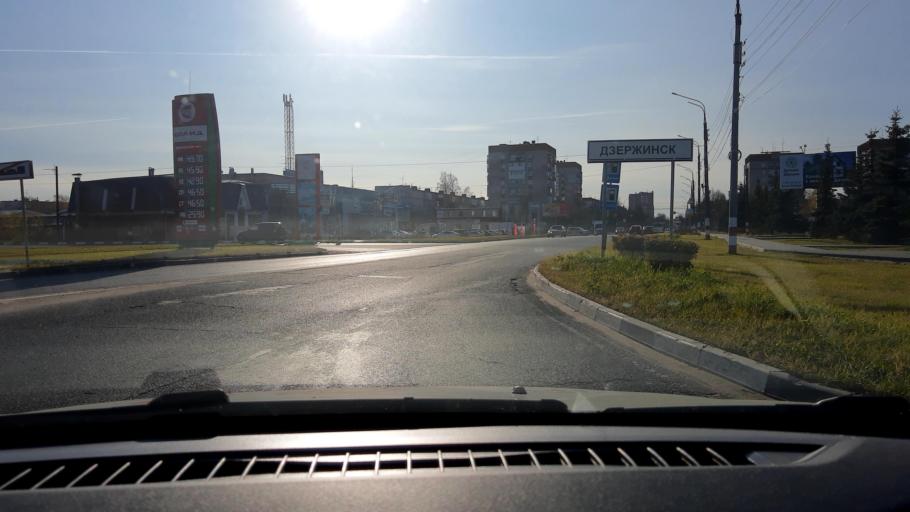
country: RU
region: Nizjnij Novgorod
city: Dzerzhinsk
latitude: 56.2574
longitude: 43.4673
